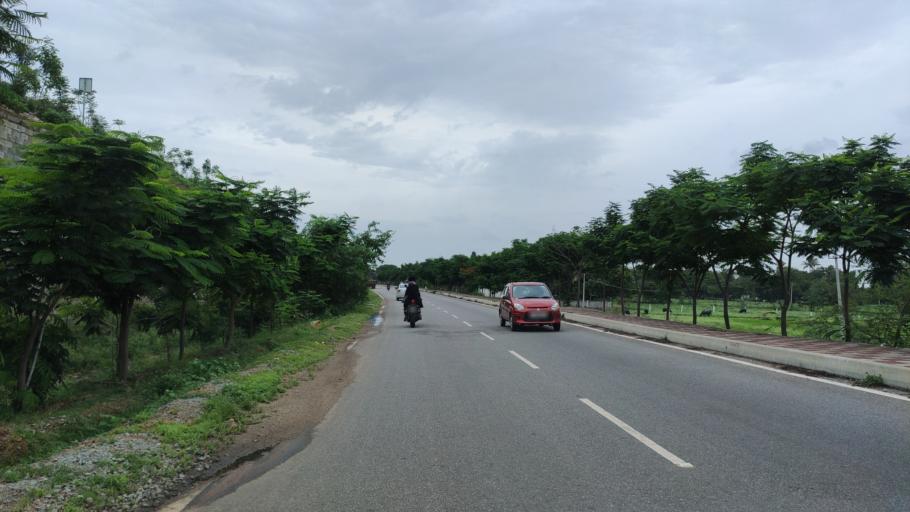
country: IN
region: Telangana
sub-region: Rangareddi
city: Secunderabad
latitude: 17.5795
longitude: 78.5931
